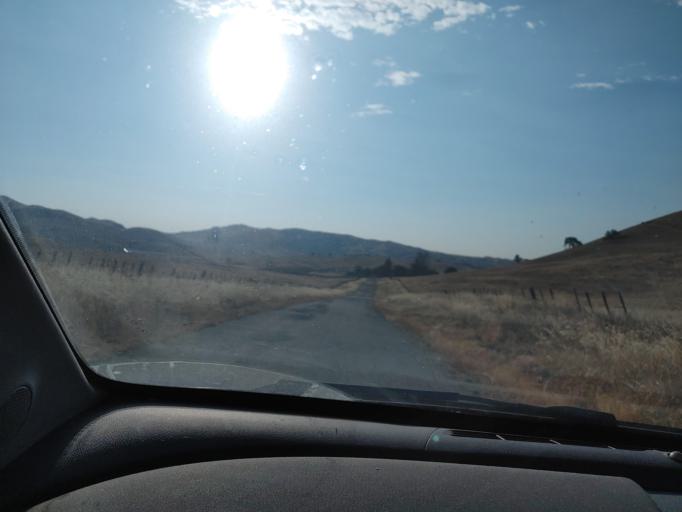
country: US
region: California
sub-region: San Benito County
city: Ridgemark
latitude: 36.7684
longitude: -121.1896
